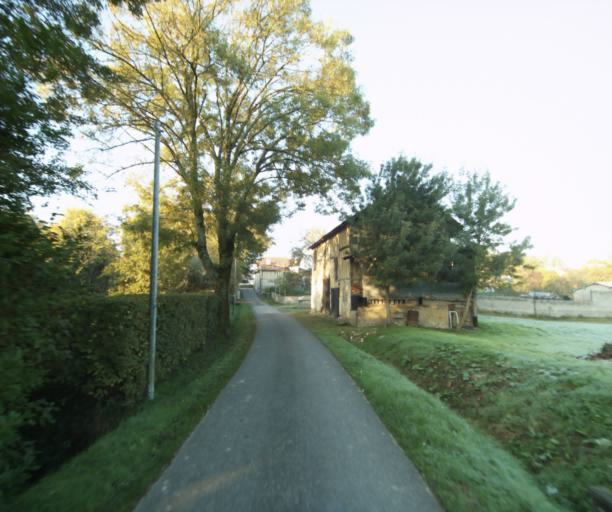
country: FR
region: Midi-Pyrenees
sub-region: Departement du Gers
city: Eauze
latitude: 43.7661
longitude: 0.1681
